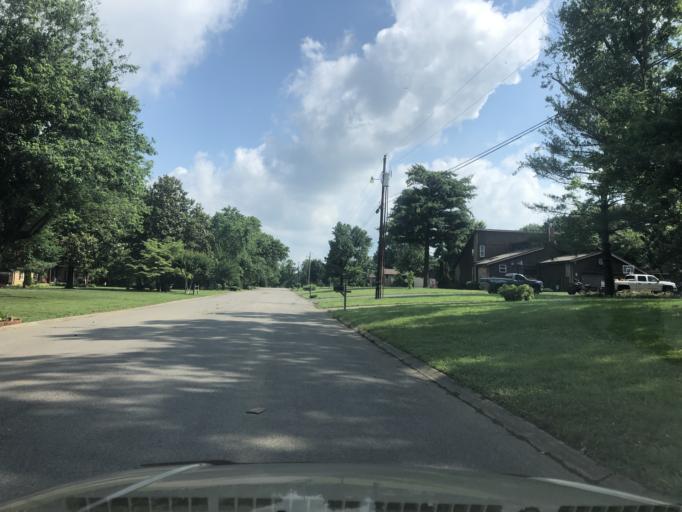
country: US
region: Tennessee
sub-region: Wilson County
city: Green Hill
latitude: 36.2331
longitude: -86.5864
